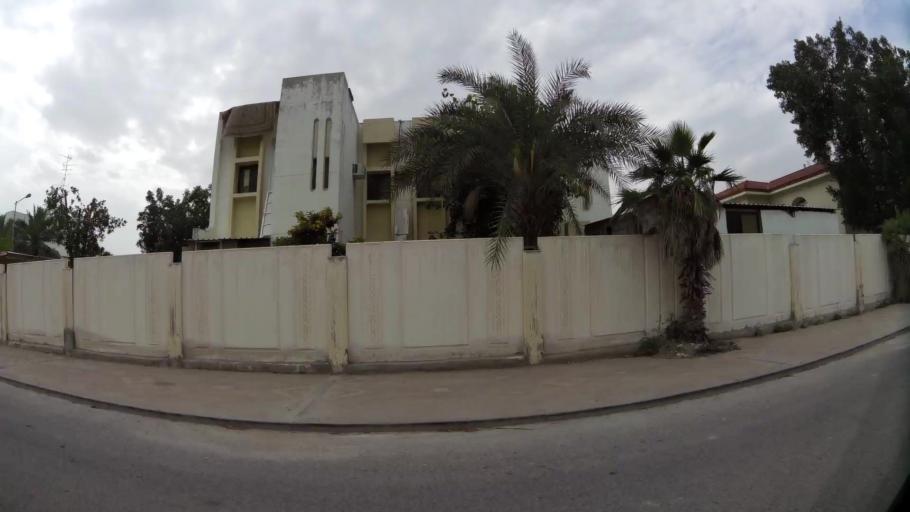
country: QA
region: Baladiyat ad Dawhah
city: Doha
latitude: 25.3345
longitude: 51.5053
